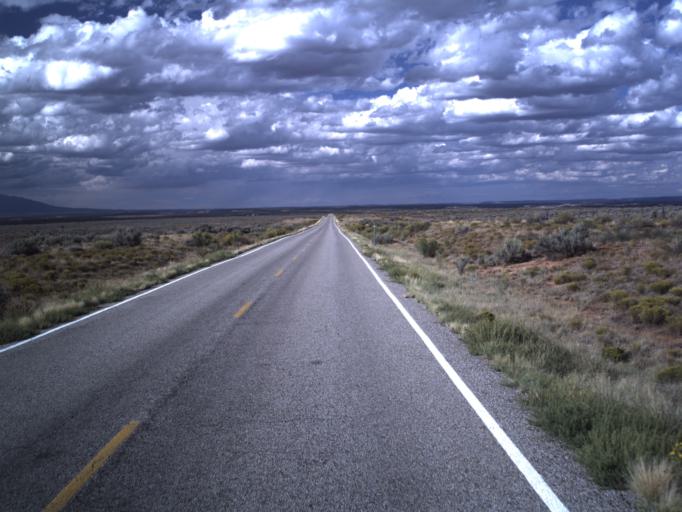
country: US
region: Utah
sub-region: San Juan County
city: Blanding
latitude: 37.3644
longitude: -109.3446
